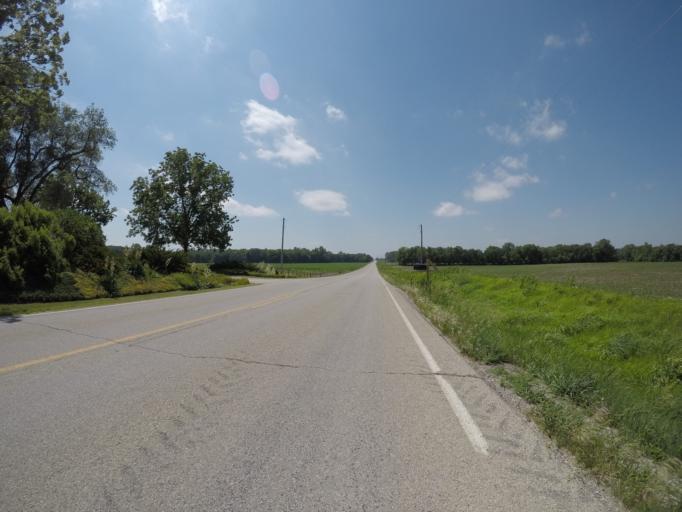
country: US
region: Kansas
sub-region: Pottawatomie County
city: Westmoreland
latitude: 39.3470
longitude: -96.4360
